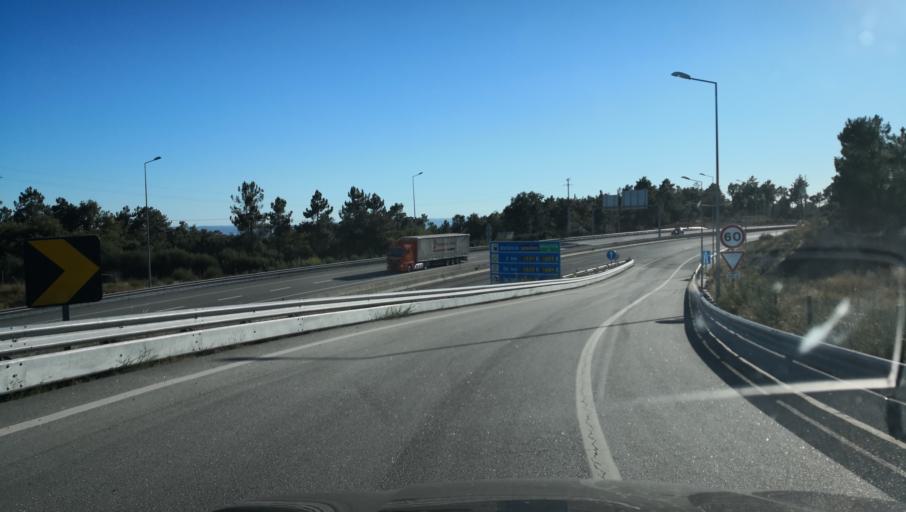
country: PT
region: Vila Real
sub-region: Sabrosa
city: Sabrosa
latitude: 41.3270
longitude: -7.6281
